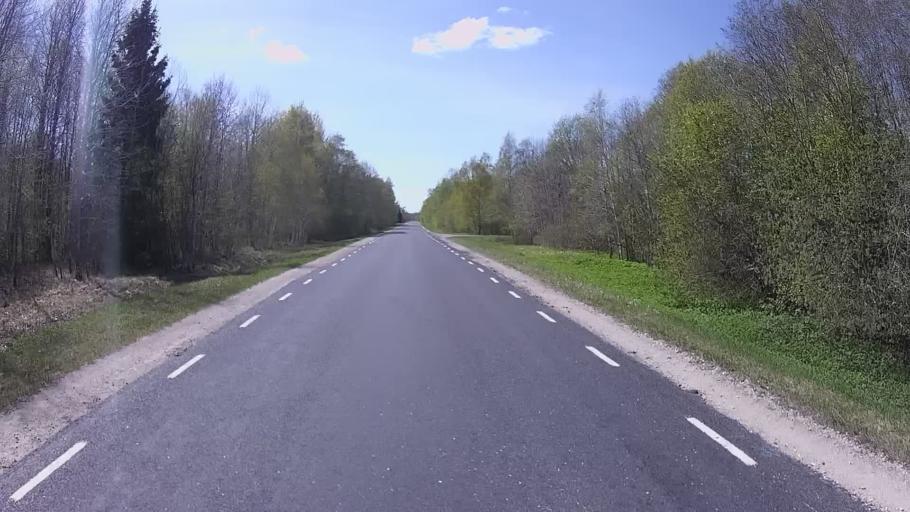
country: EE
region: Laeaene
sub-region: Ridala Parish
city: Uuemoisa
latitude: 59.0202
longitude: 23.7996
